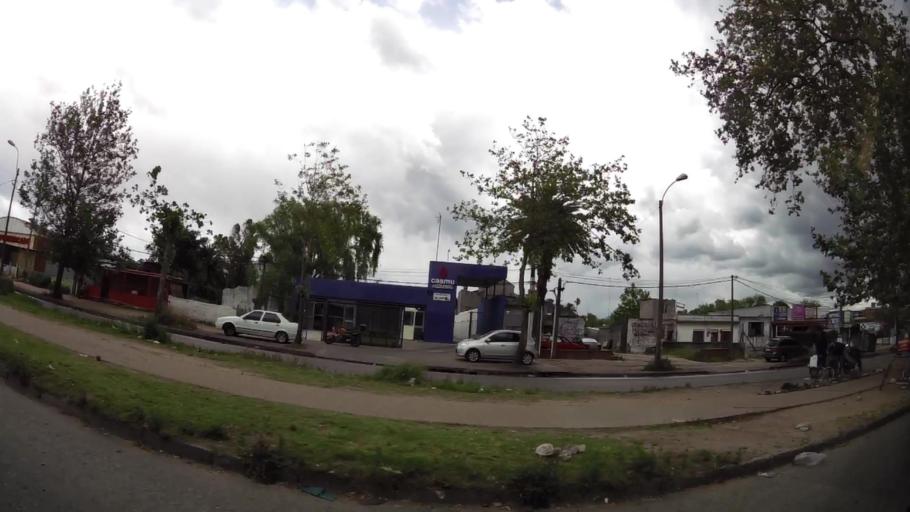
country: UY
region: Canelones
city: Toledo
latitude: -34.8180
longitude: -56.1394
